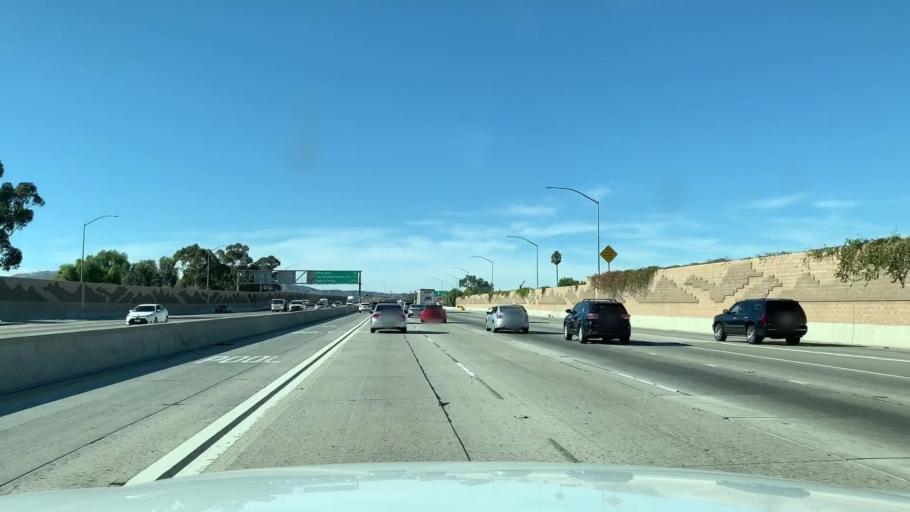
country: US
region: California
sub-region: Los Angeles County
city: San Fernando
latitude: 34.2685
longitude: -118.4452
